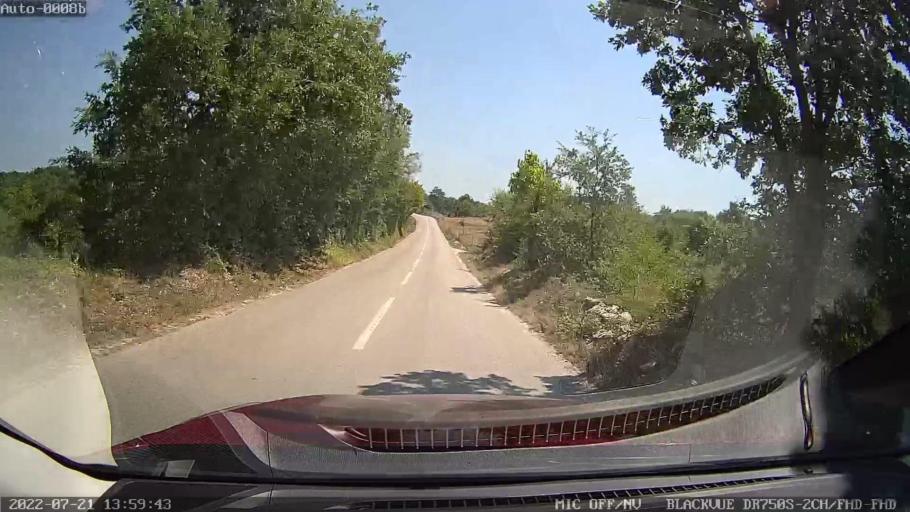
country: HR
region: Istarska
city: Vodnjan
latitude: 45.1028
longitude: 13.8641
